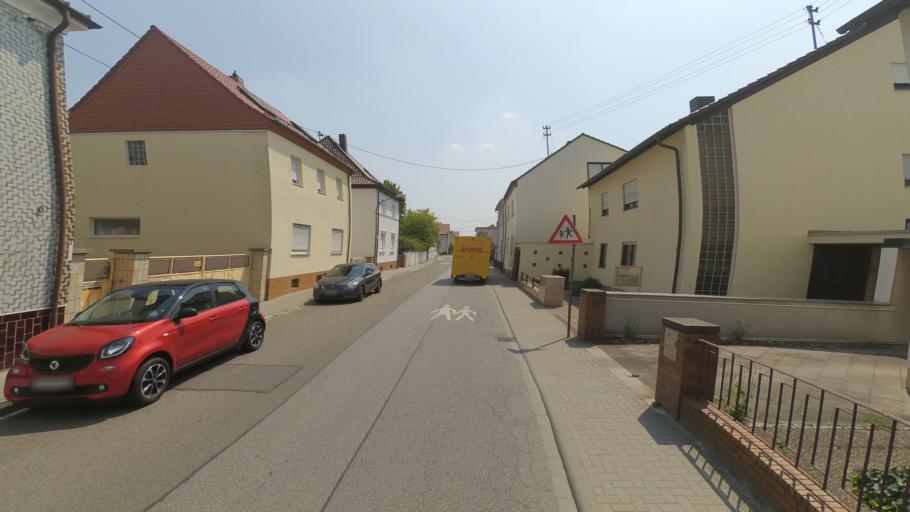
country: DE
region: Rheinland-Pfalz
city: Mutterstadt
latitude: 49.4539
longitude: 8.3753
